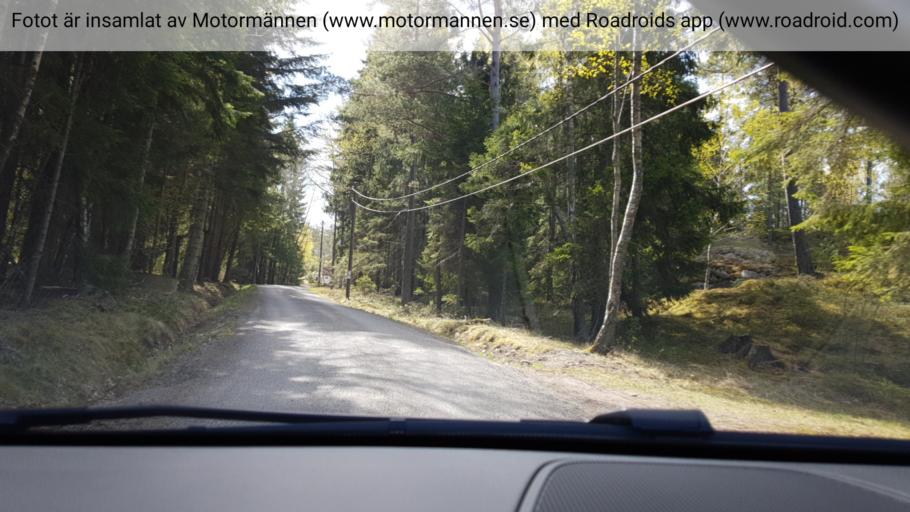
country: SE
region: Stockholm
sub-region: Haninge Kommun
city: Jordbro
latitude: 59.0186
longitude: 18.1091
